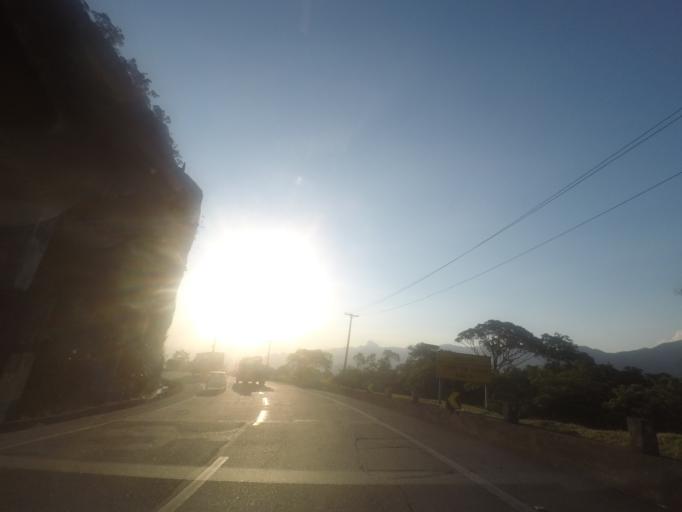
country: BR
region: Rio de Janeiro
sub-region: Petropolis
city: Petropolis
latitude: -22.5213
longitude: -43.2368
